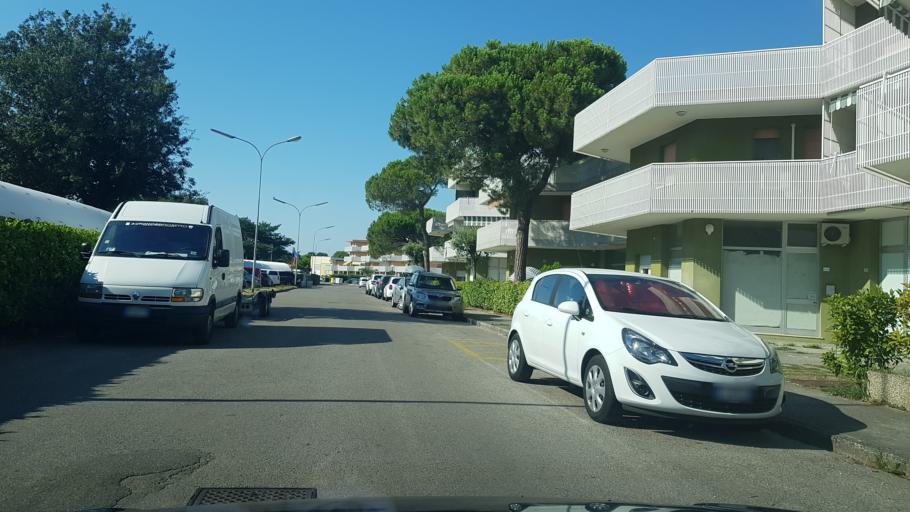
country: IT
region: Veneto
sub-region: Provincia di Venezia
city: Bibione
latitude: 45.6384
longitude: 13.0426
